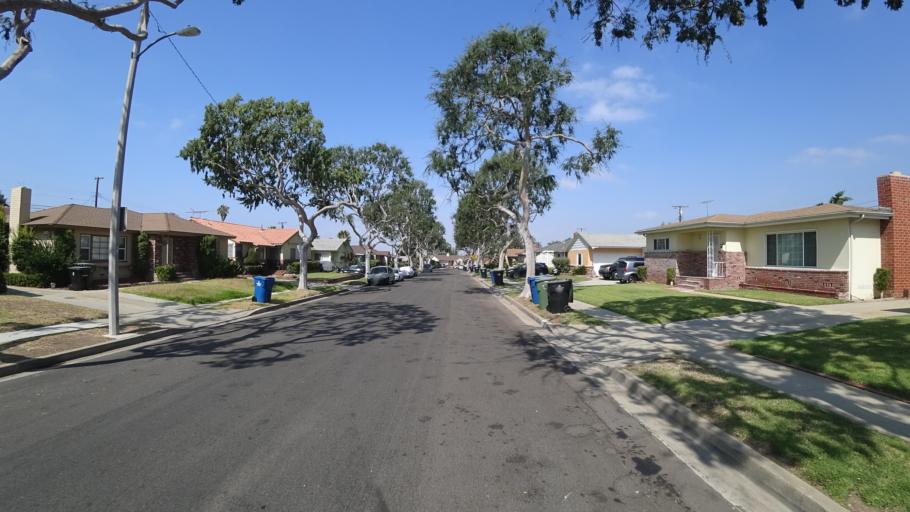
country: US
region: California
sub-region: Los Angeles County
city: West Athens
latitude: 33.9333
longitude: -118.3217
